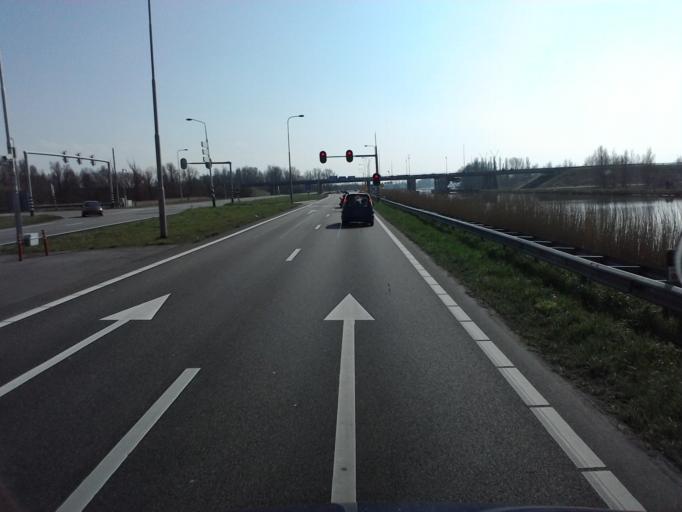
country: NL
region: North Holland
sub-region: Gemeente Zaanstad
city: Zaanstad
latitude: 52.4771
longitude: 4.7702
